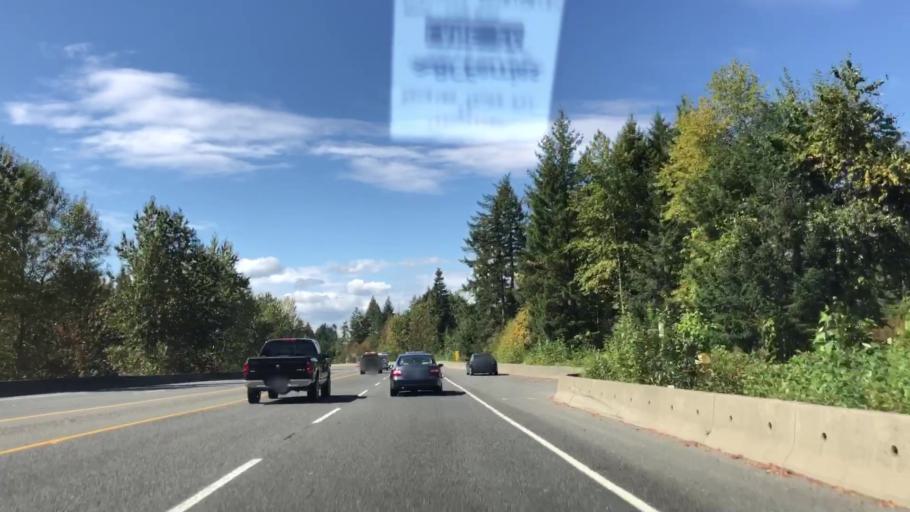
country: CA
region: British Columbia
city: Nanaimo
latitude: 49.1170
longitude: -123.8691
